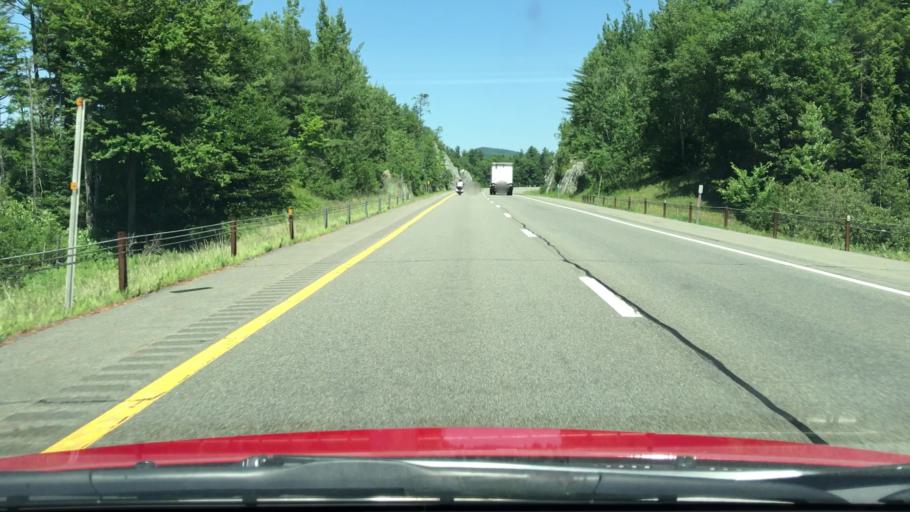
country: US
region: New York
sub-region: Essex County
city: Elizabethtown
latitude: 44.3321
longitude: -73.5323
